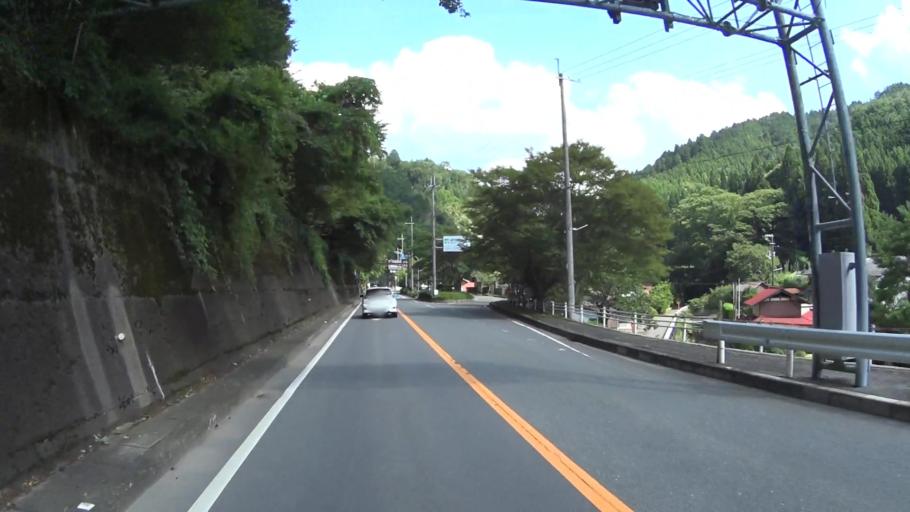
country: JP
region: Kyoto
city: Kameoka
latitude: 35.1208
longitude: 135.6517
